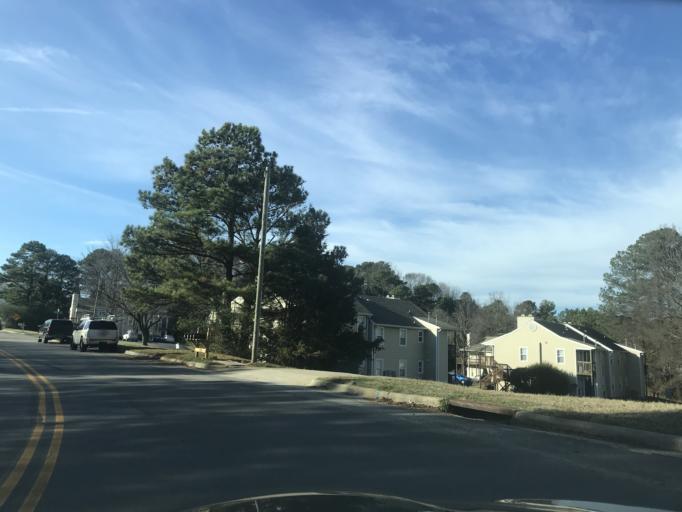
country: US
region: North Carolina
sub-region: Wake County
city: Cary
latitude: 35.7853
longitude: -78.7406
